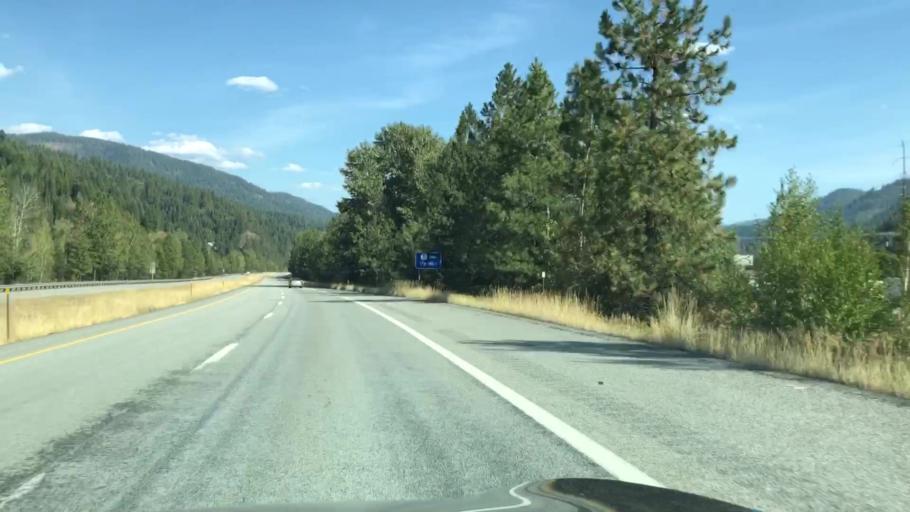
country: US
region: Idaho
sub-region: Shoshone County
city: Osburn
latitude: 47.5097
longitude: -116.0116
